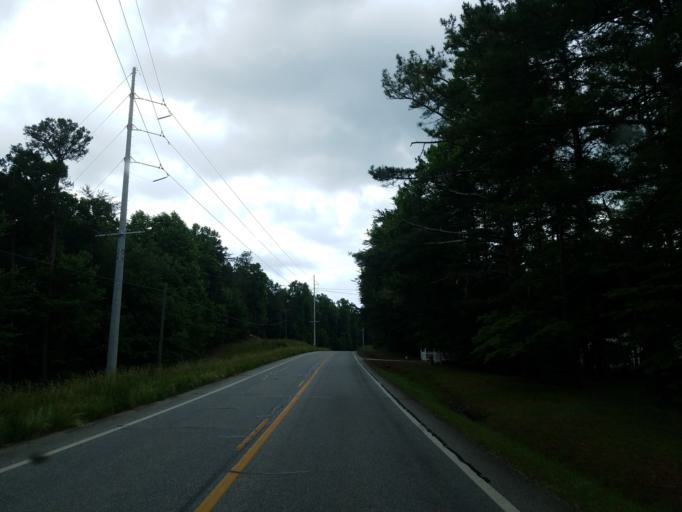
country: US
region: Georgia
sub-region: Dawson County
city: Dawsonville
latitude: 34.4384
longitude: -84.1633
